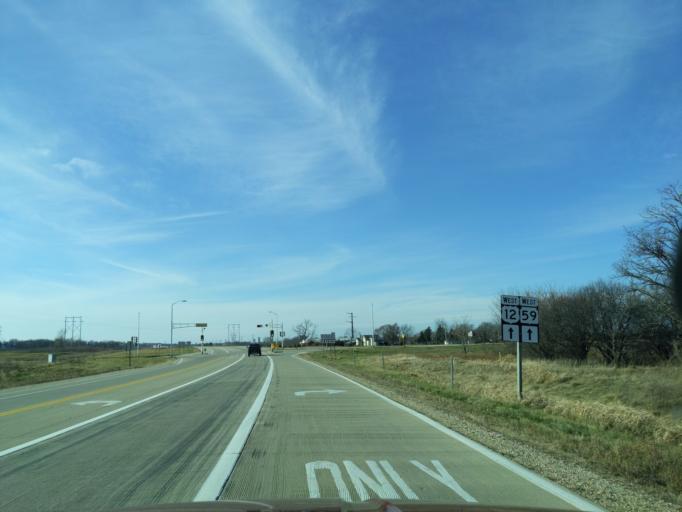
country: US
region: Wisconsin
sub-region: Walworth County
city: Whitewater
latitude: 42.8197
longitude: -88.6987
